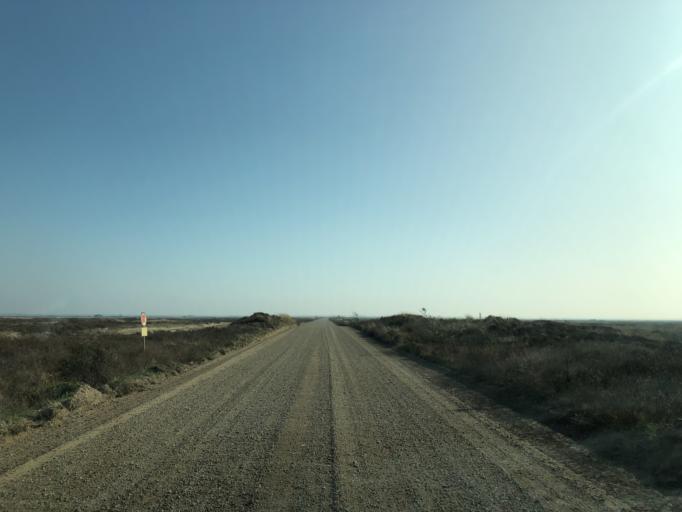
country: DK
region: South Denmark
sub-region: Varde Kommune
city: Oksbol
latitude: 55.5979
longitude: 8.1545
